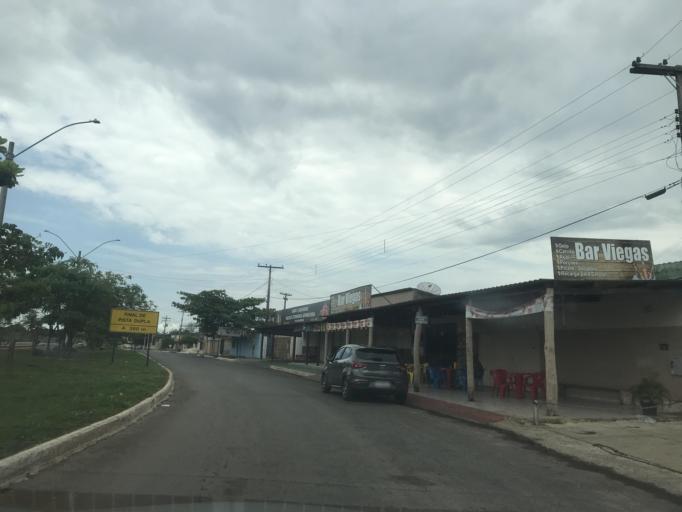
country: BR
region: Goias
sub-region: Luziania
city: Luziania
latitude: -16.2563
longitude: -47.9627
